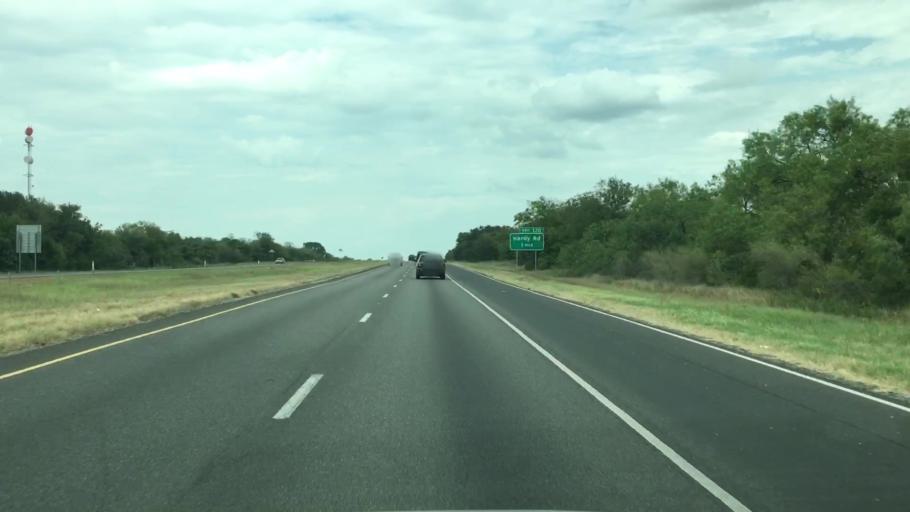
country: US
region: Texas
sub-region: Atascosa County
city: Poteet
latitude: 29.1234
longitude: -98.4308
